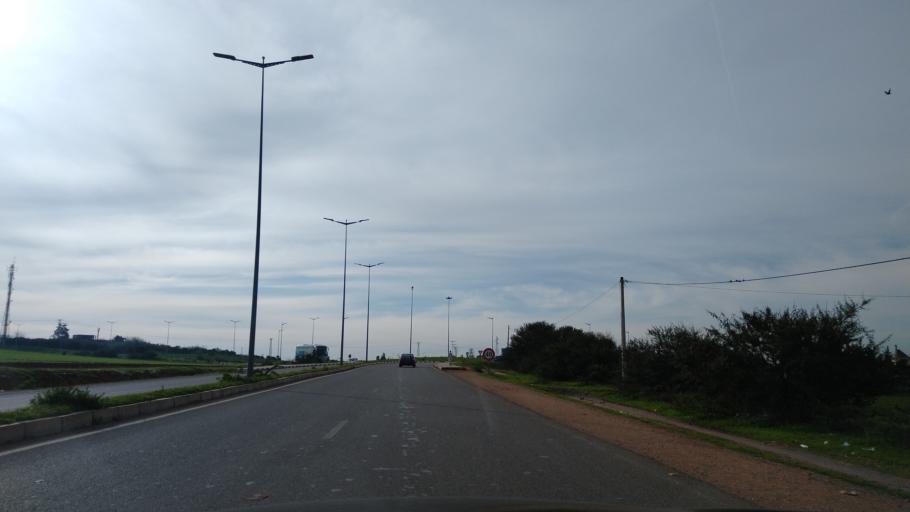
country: MA
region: Rabat-Sale-Zemmour-Zaer
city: Sale
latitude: 33.9855
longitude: -6.7397
